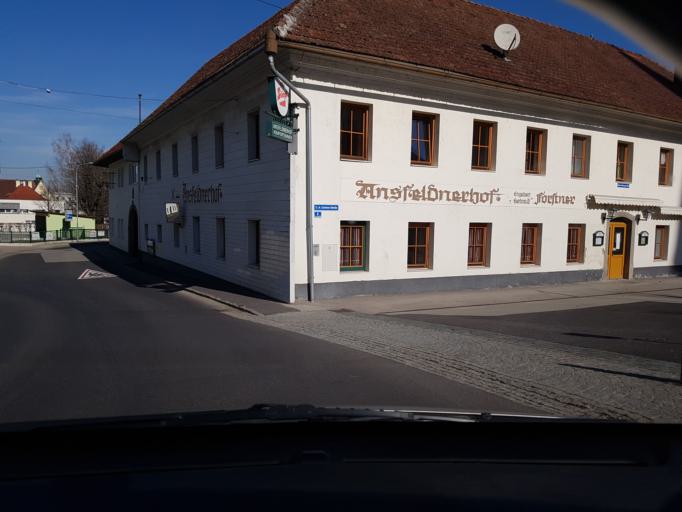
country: AT
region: Upper Austria
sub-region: Politischer Bezirk Linz-Land
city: Ansfelden
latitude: 48.2097
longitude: 14.2898
